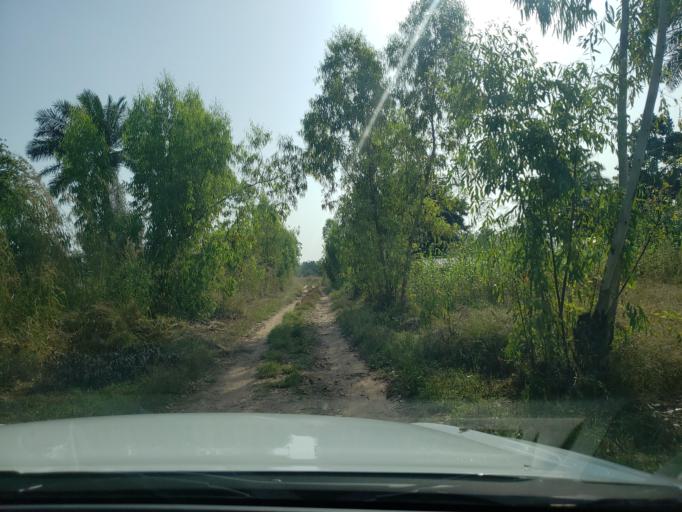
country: TG
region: Kara
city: Bafilo
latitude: 9.4104
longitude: 1.1792
